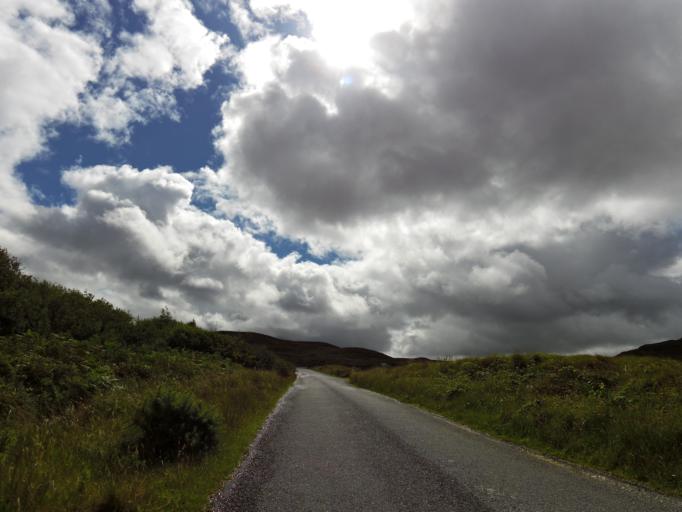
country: IE
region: Connaught
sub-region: County Galway
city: Oughterard
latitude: 53.3992
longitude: -9.3320
